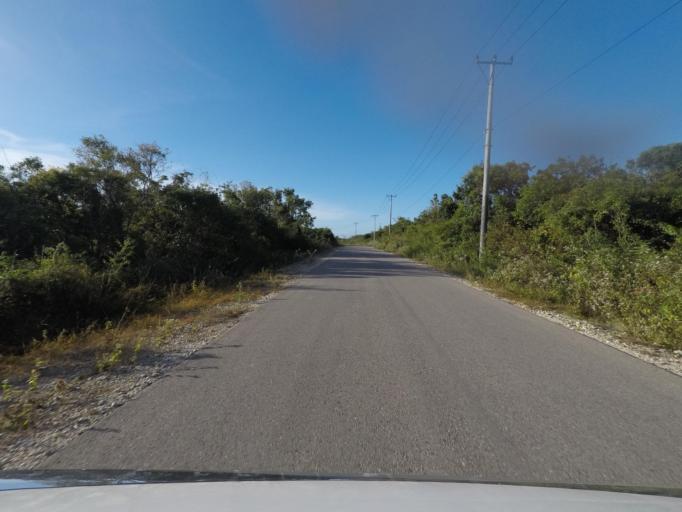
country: TL
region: Lautem
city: Lospalos
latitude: -8.3857
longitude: 127.0132
